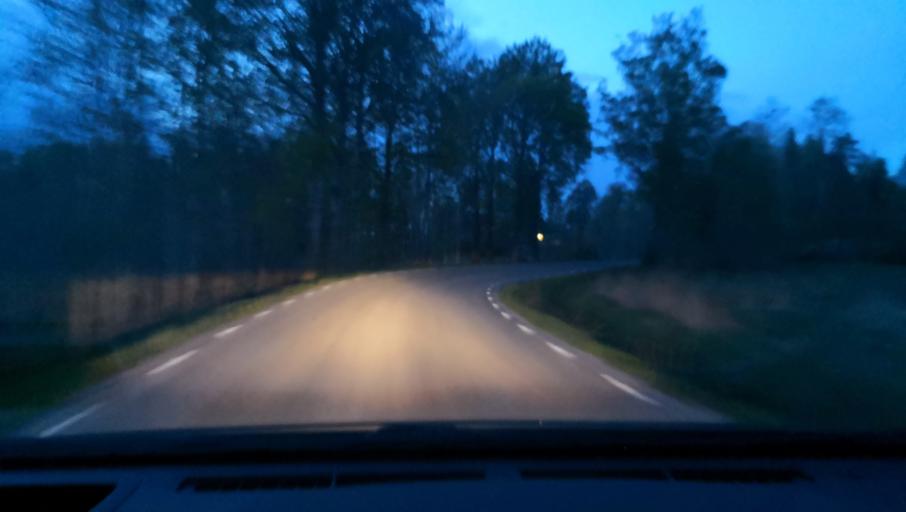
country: SE
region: OErebro
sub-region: Orebro Kommun
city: Vintrosa
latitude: 59.1871
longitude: 15.0418
